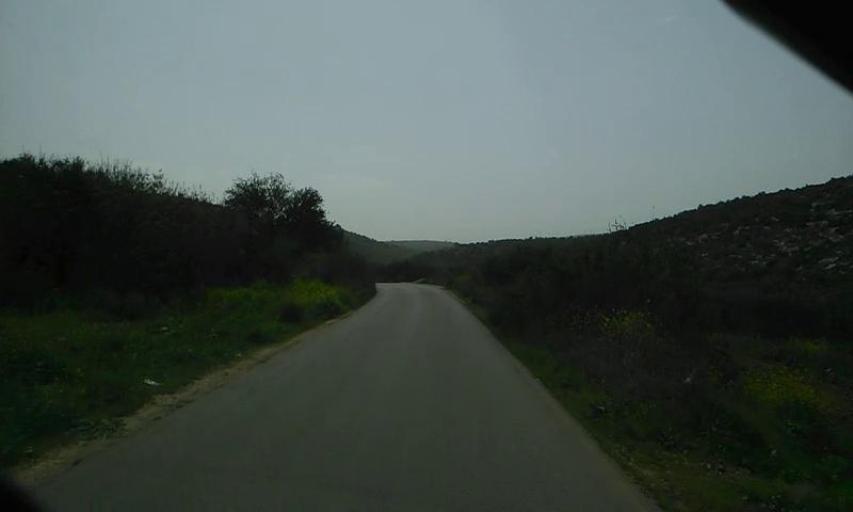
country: PS
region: West Bank
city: Silat al Harithiyah
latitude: 32.5150
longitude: 35.2153
